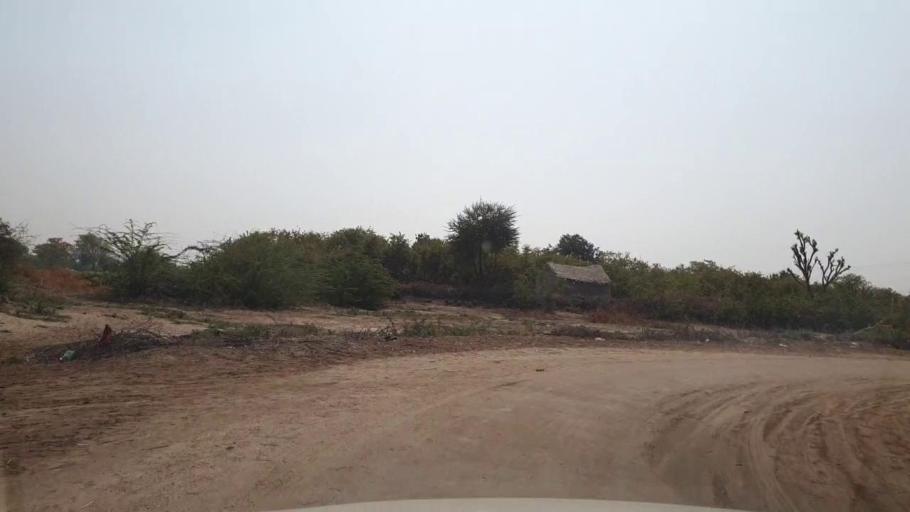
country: PK
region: Sindh
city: Umarkot
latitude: 25.4391
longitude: 69.6786
